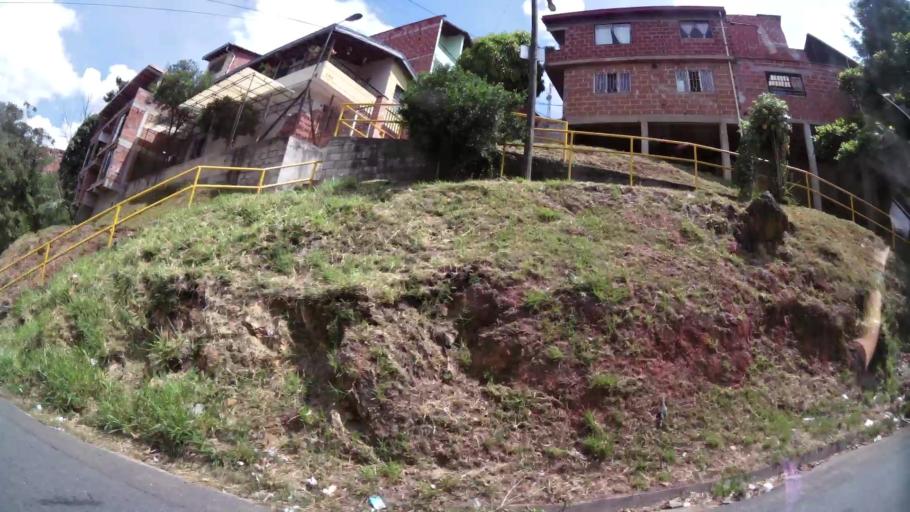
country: CO
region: Antioquia
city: Bello
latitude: 6.3459
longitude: -75.5514
